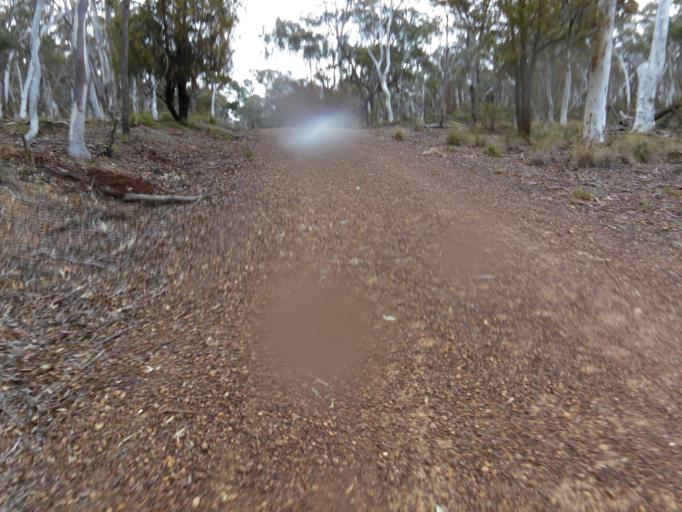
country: AU
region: Australian Capital Territory
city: Acton
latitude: -35.2641
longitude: 149.0967
